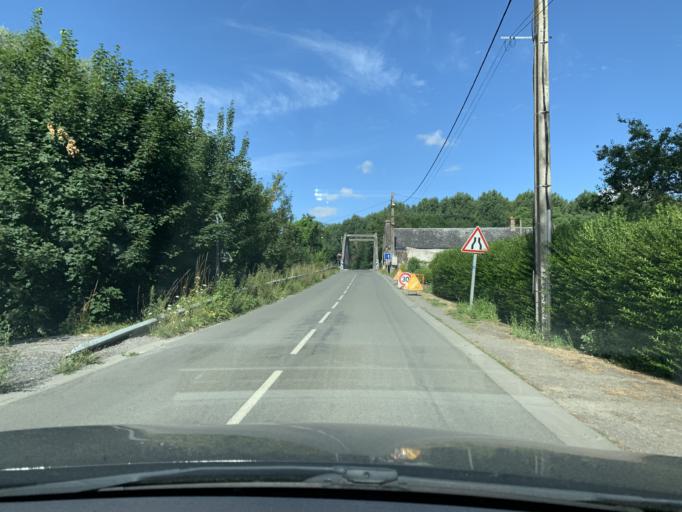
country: FR
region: Nord-Pas-de-Calais
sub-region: Departement du Nord
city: Proville
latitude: 50.1543
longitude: 3.1862
